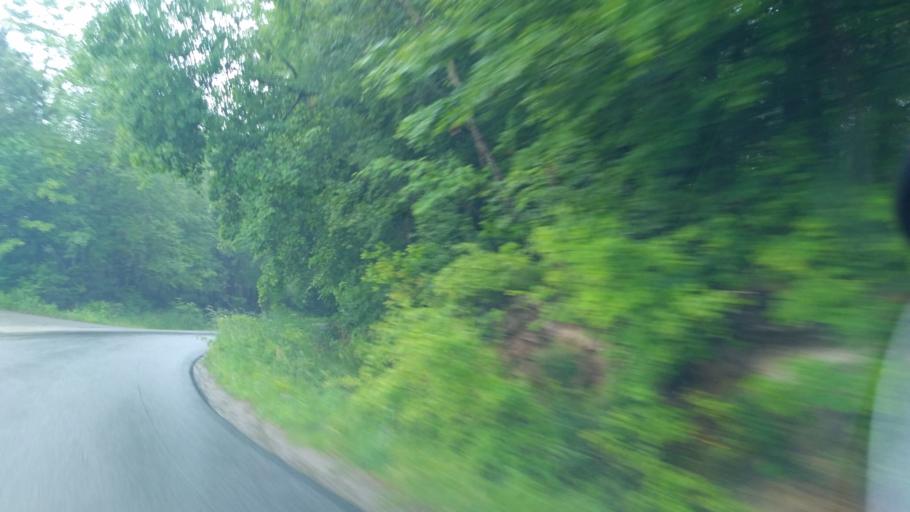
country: PL
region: Subcarpathian Voivodeship
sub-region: Powiat jasielski
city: Jaslo
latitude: 49.7850
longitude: 21.4897
